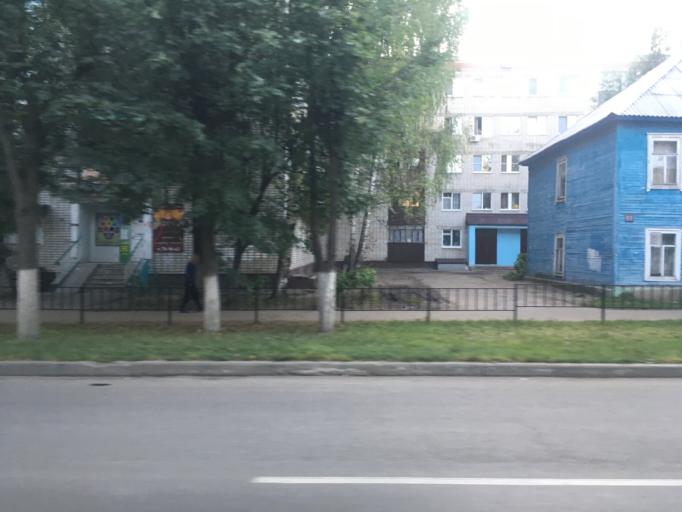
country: RU
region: Mariy-El
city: Yoshkar-Ola
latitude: 56.6442
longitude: 47.8911
